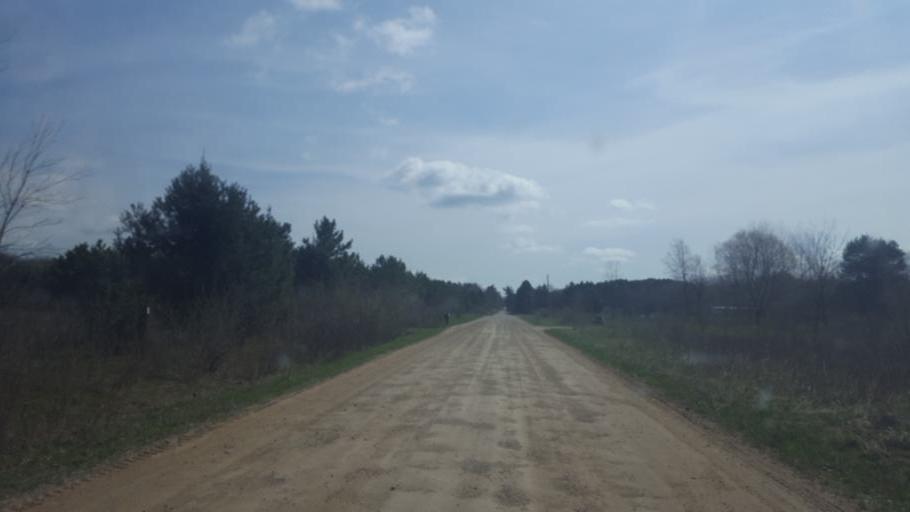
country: US
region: Michigan
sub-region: Montcalm County
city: Edmore
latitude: 43.4592
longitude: -84.9403
